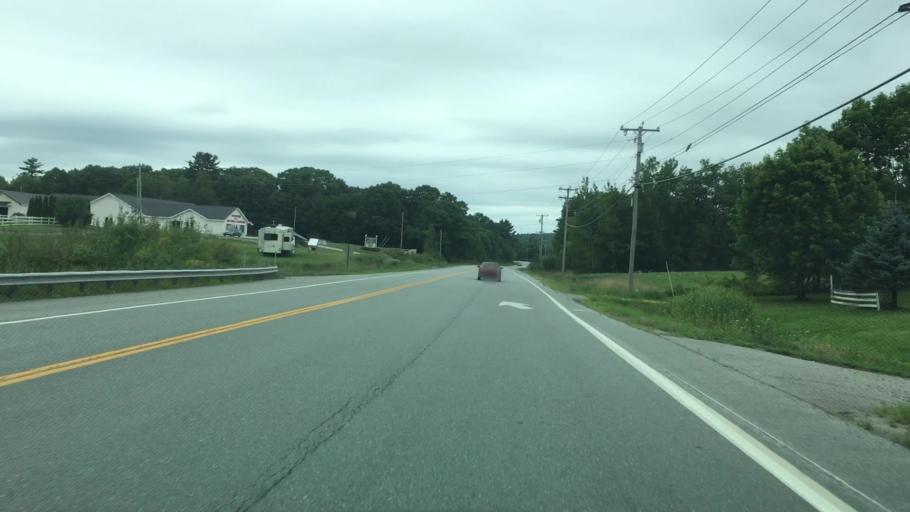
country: US
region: Maine
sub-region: Waldo County
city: Frankfort
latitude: 44.6141
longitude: -68.8693
